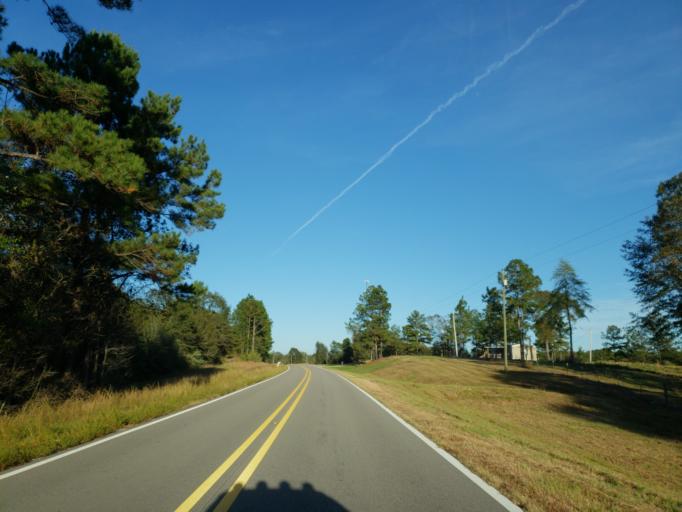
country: US
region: Mississippi
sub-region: Perry County
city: Richton
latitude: 31.3559
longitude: -88.7438
